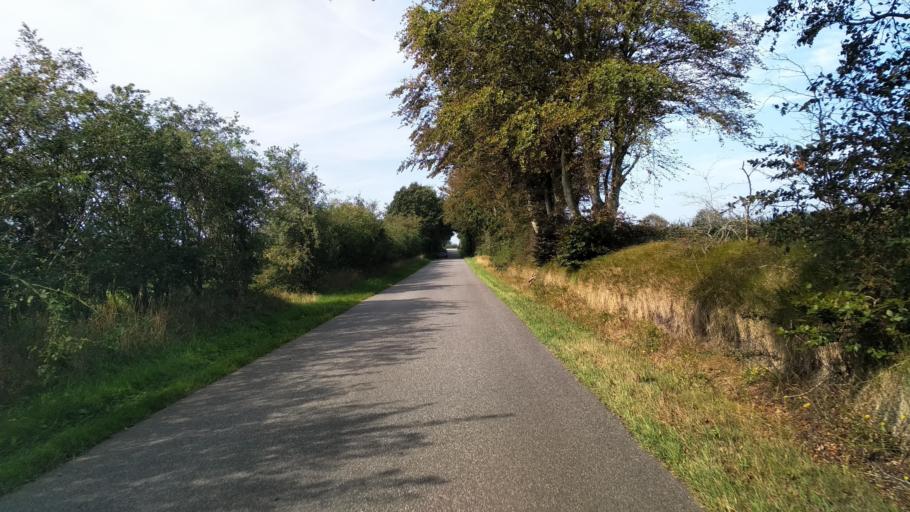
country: DE
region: Schleswig-Holstein
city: Bordelum
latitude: 54.6412
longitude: 8.9536
